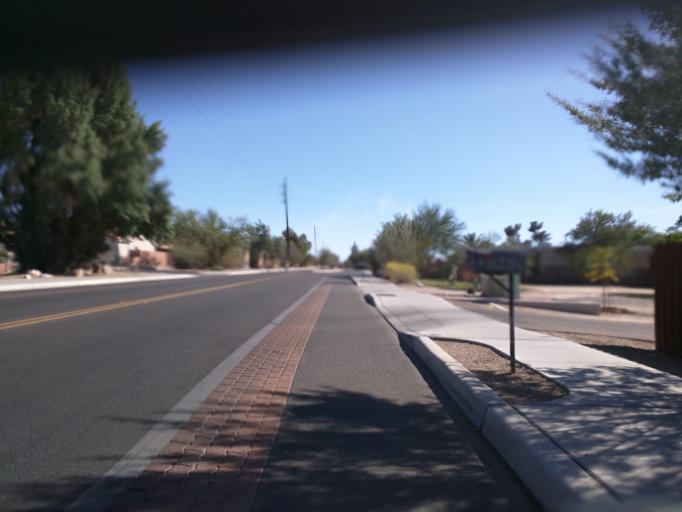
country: US
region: Arizona
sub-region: Pima County
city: Catalina Foothills
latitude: 32.2784
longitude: -110.9524
